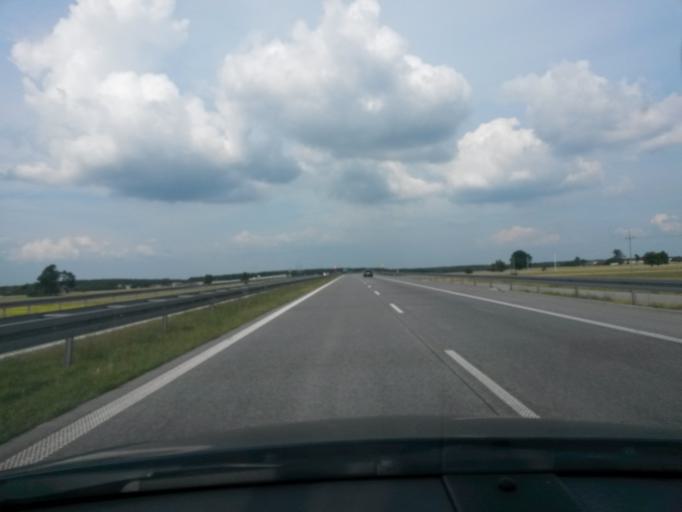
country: PL
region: Lodz Voivodeship
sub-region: Powiat tomaszowski
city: Lubochnia
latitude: 51.6163
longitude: 20.0834
